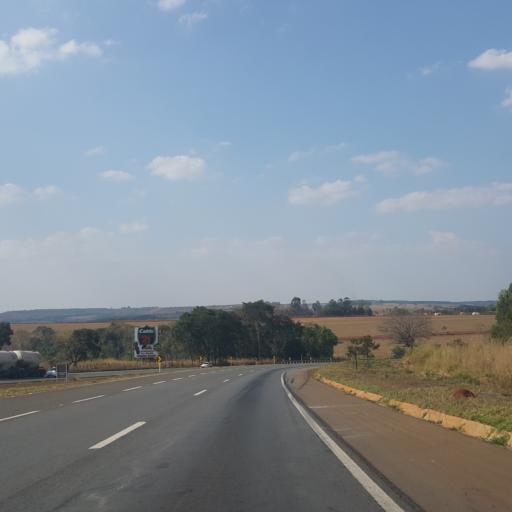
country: BR
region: Goias
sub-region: Abadiania
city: Abadiania
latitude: -16.2794
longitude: -48.7900
